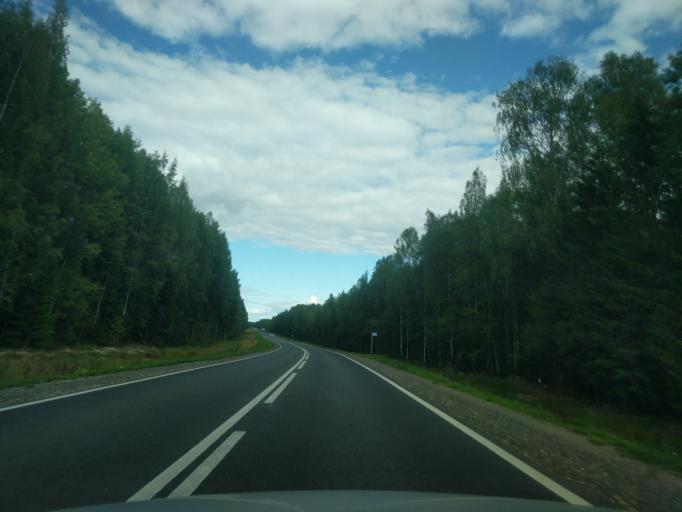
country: RU
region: Kostroma
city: Kadyy
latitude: 57.8422
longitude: 43.4453
